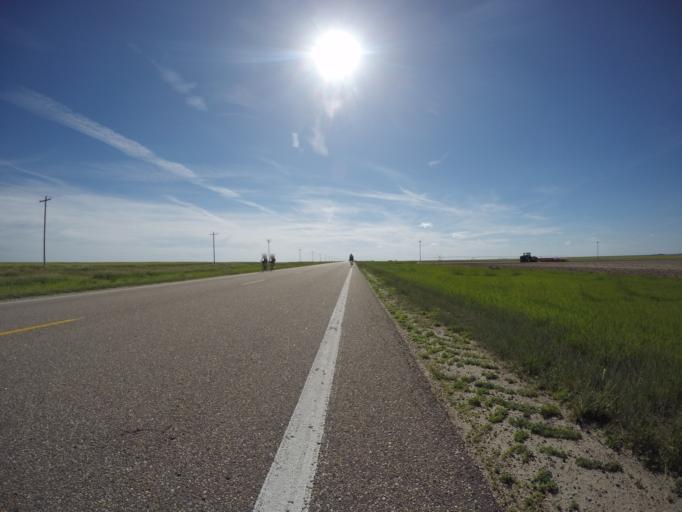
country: US
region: Kansas
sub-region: Cheyenne County
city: Saint Francis
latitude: 39.7566
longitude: -102.0016
